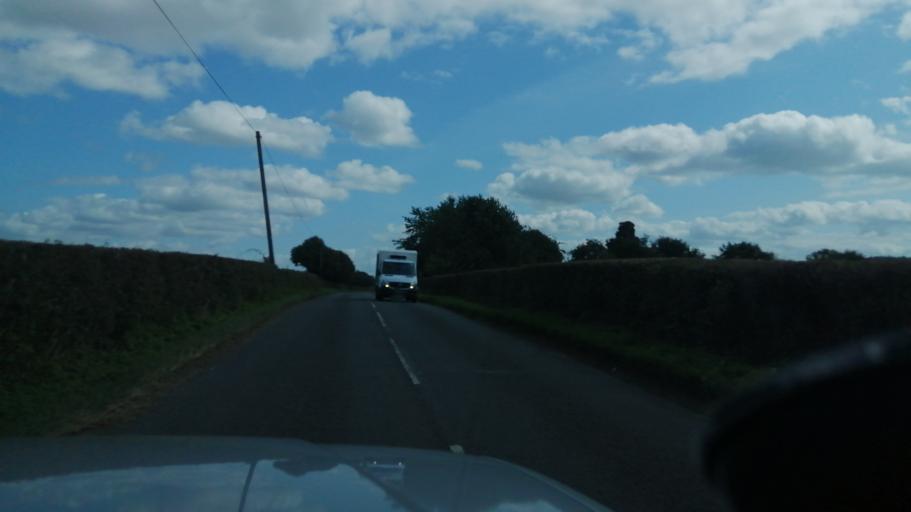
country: GB
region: England
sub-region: Herefordshire
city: Kingstone
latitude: 52.0144
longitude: -2.8382
